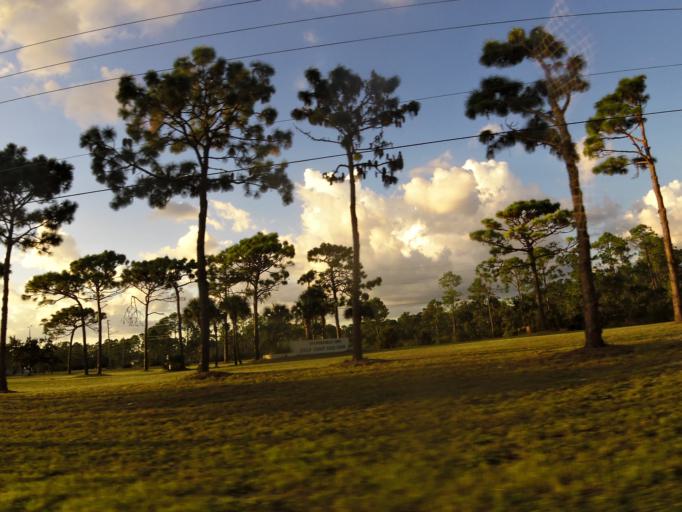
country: US
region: Florida
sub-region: Gulf County
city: Port Saint Joe
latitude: 29.7765
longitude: -85.2810
